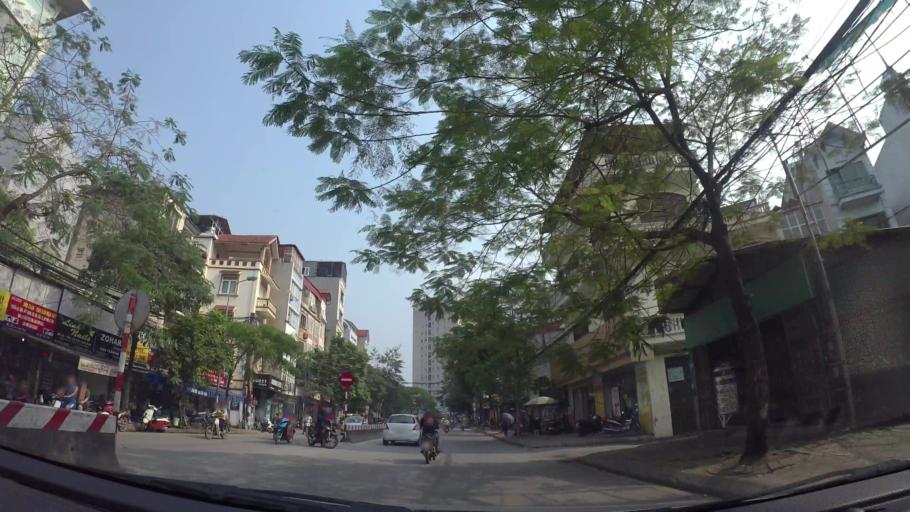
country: VN
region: Ha Noi
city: Tay Ho
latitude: 21.0537
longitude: 105.8087
